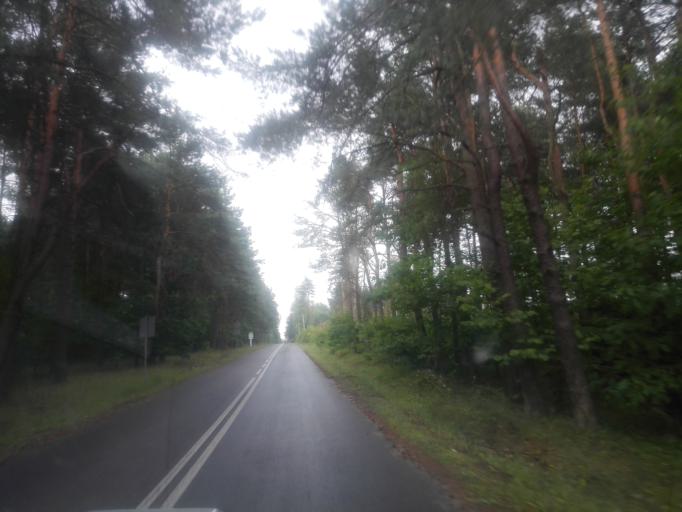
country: PL
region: Silesian Voivodeship
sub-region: Powiat myszkowski
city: Choron
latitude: 50.7078
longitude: 19.3391
